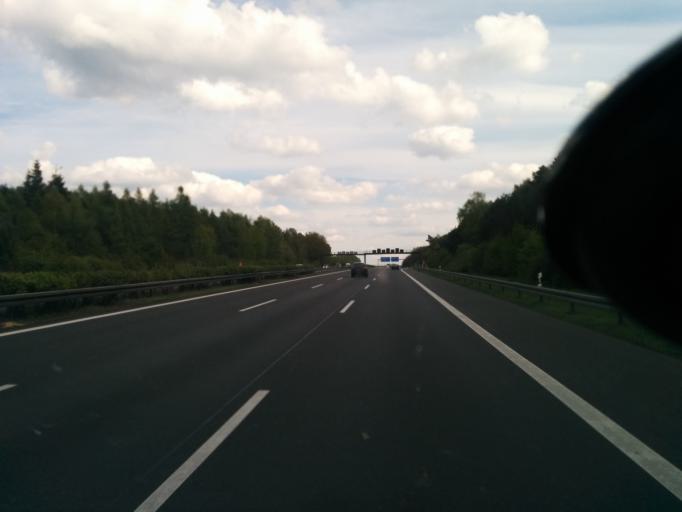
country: DE
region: Brandenburg
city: Fichtenwalde
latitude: 52.2992
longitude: 12.8983
